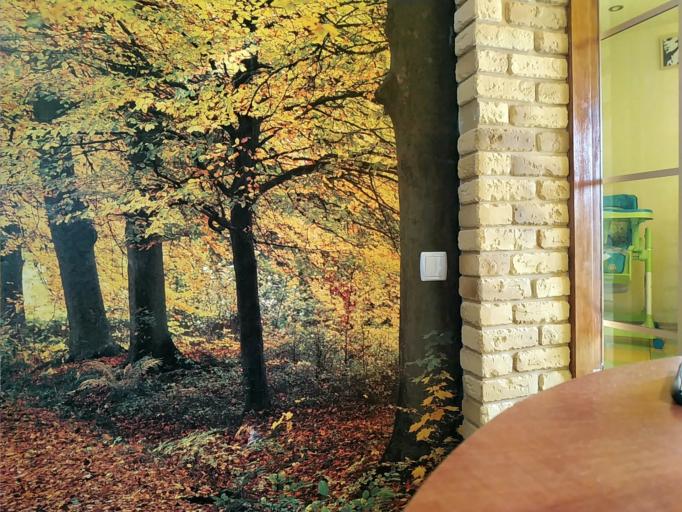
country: RU
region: Novgorod
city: Parfino
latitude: 57.7985
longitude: 31.6201
